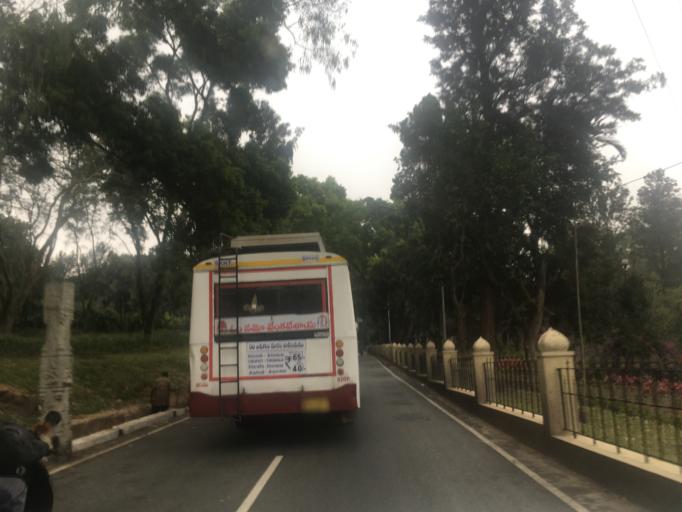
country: IN
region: Andhra Pradesh
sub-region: Chittoor
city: Tirumala
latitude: 13.6706
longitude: 79.3508
